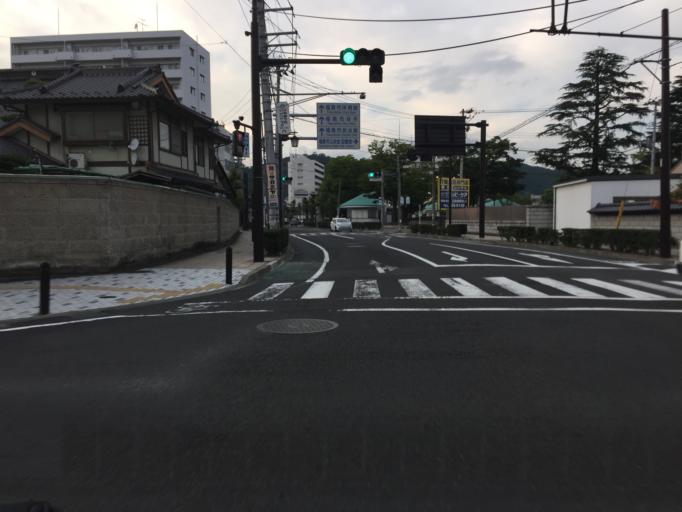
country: JP
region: Fukushima
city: Fukushima-shi
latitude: 37.7570
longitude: 140.4681
